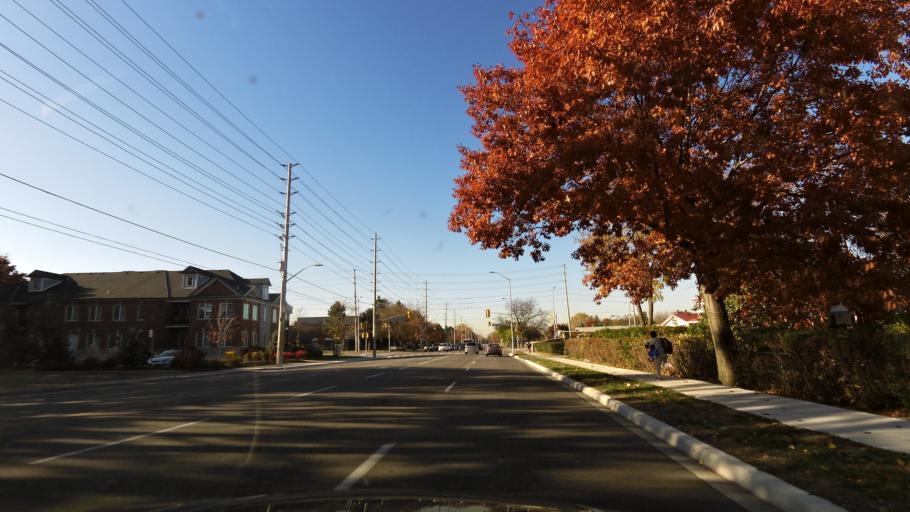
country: CA
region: Ontario
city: Etobicoke
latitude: 43.6069
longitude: -79.6025
